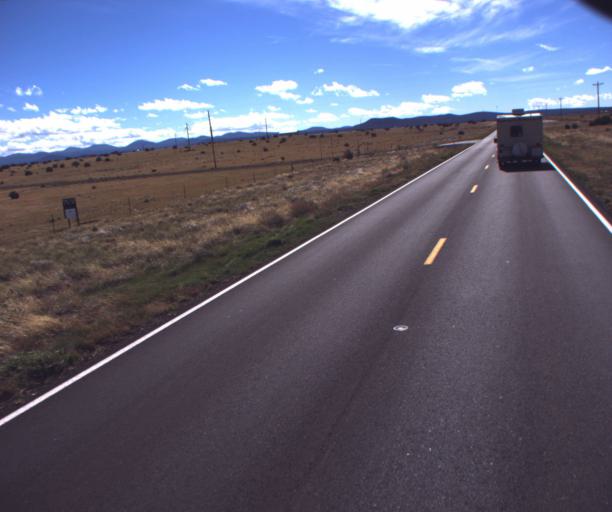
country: US
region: Arizona
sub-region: Navajo County
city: White Mountain Lake
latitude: 34.3732
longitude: -109.6912
